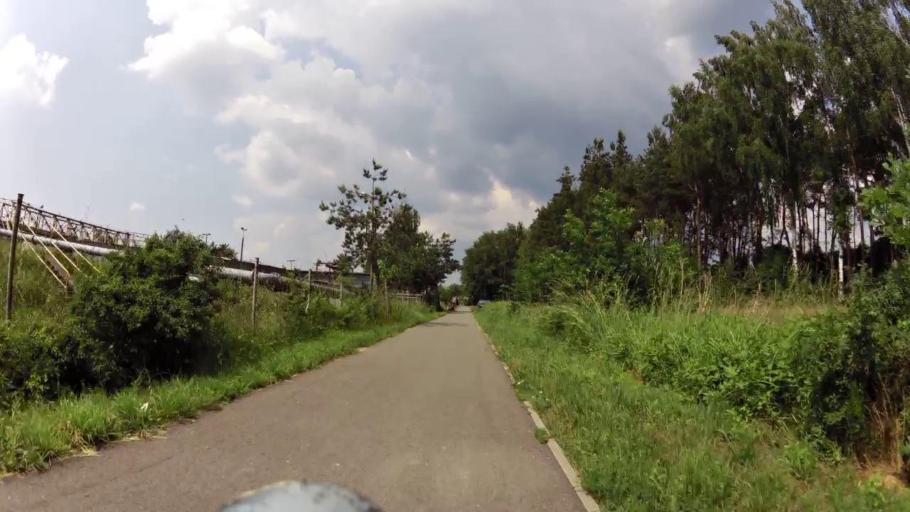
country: PL
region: Kujawsko-Pomorskie
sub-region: Powiat bydgoski
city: Koronowo
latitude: 53.3014
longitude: 17.9462
